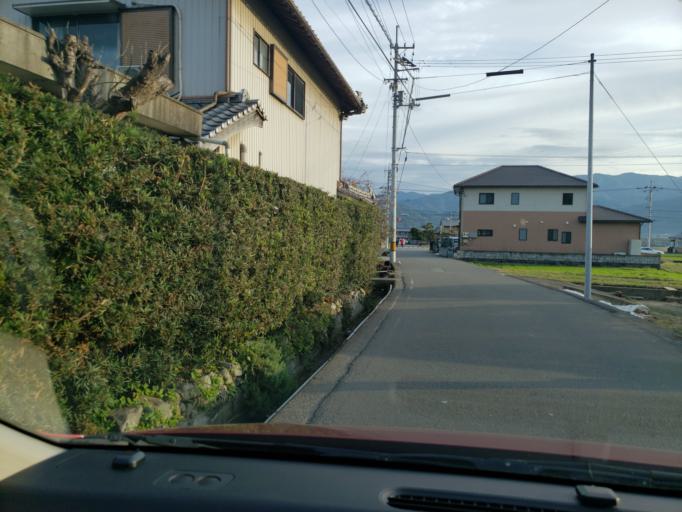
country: JP
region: Tokushima
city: Wakimachi
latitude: 34.0833
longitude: 134.2271
